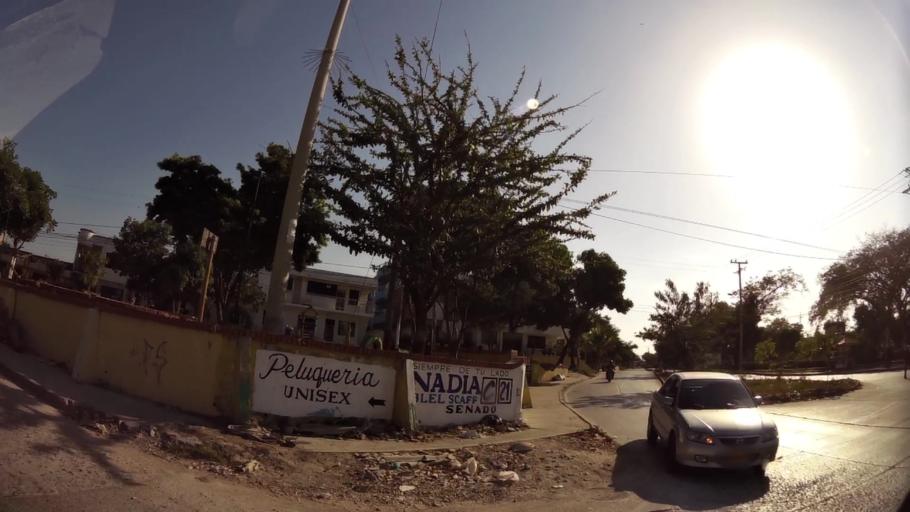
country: CO
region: Bolivar
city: Cartagena
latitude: 10.3838
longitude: -75.4859
